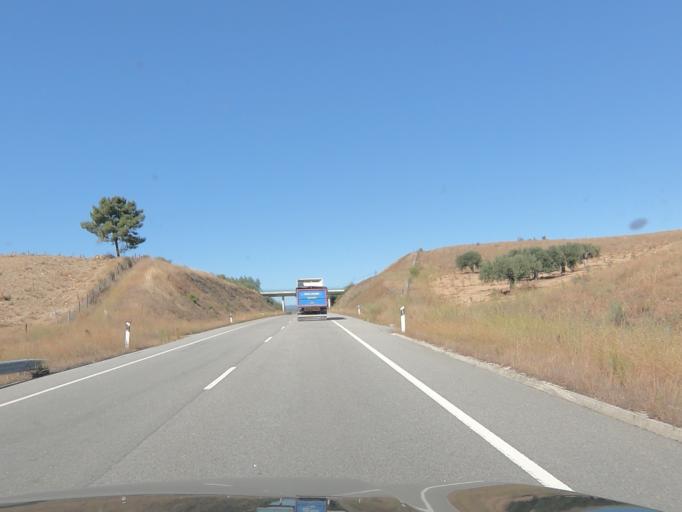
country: PT
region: Braganca
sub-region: Mirandela
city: Mirandela
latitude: 41.5268
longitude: -7.2425
